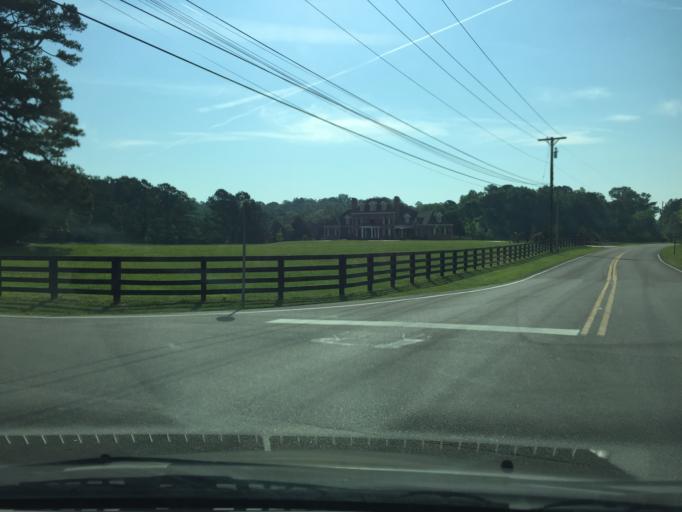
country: US
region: Tennessee
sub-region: Hamilton County
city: Collegedale
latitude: 35.0584
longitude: -85.0156
